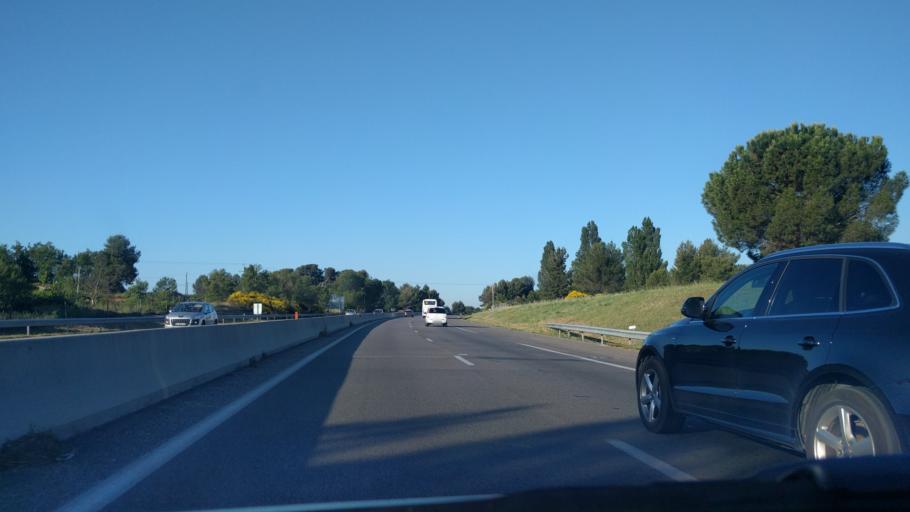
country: FR
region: Provence-Alpes-Cote d'Azur
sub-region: Departement des Bouches-du-Rhone
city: Venelles
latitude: 43.5786
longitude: 5.4746
